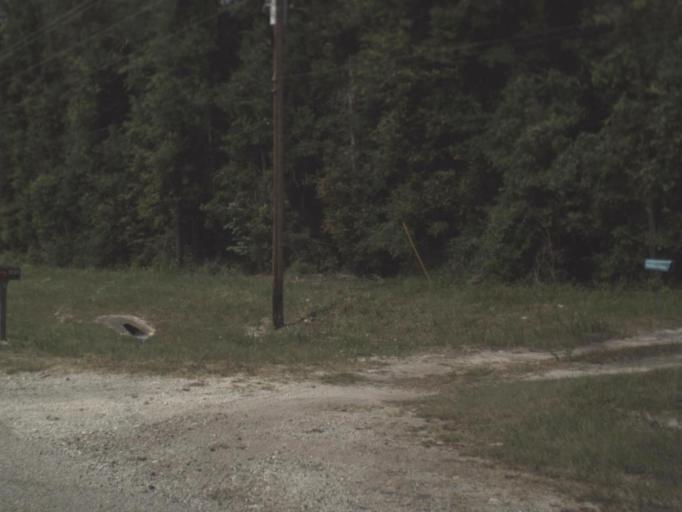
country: US
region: Florida
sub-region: Clay County
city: Green Cove Springs
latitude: 29.9161
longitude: -81.6806
